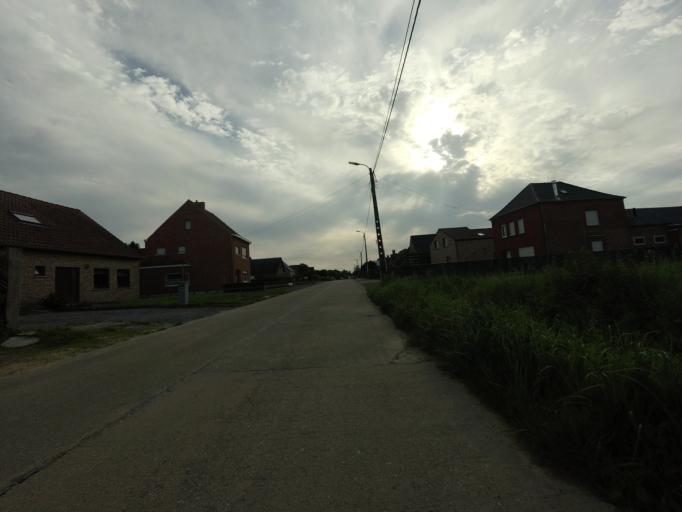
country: BE
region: Flanders
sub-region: Provincie Vlaams-Brabant
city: Boortmeerbeek
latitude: 50.9698
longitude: 4.5925
